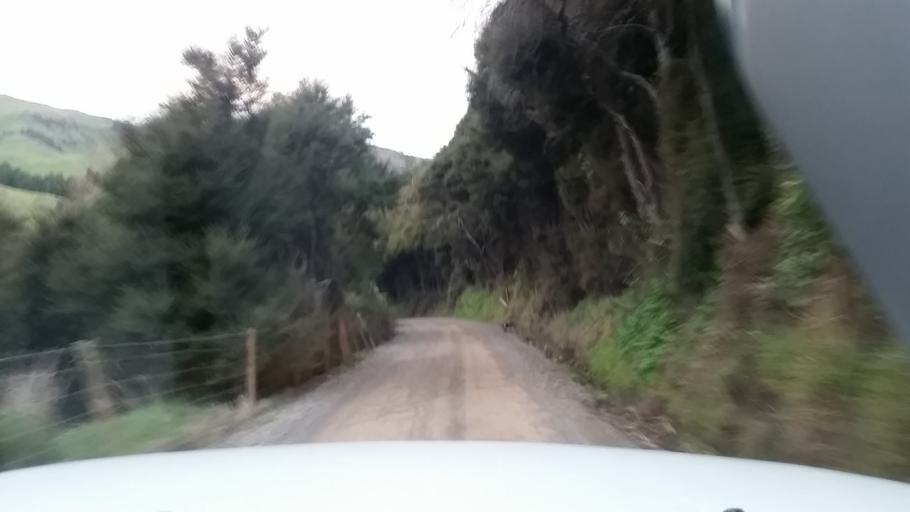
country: NZ
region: Canterbury
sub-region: Christchurch City
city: Christchurch
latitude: -43.7368
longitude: 172.7898
